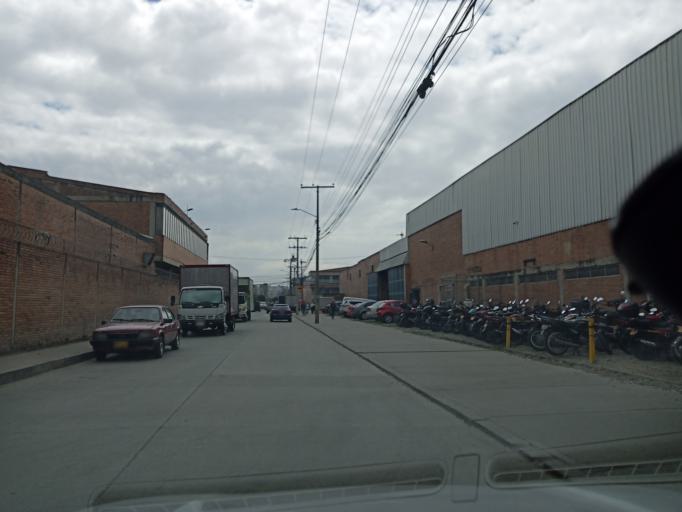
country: CO
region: Bogota D.C.
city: Bogota
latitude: 4.6507
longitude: -74.1214
